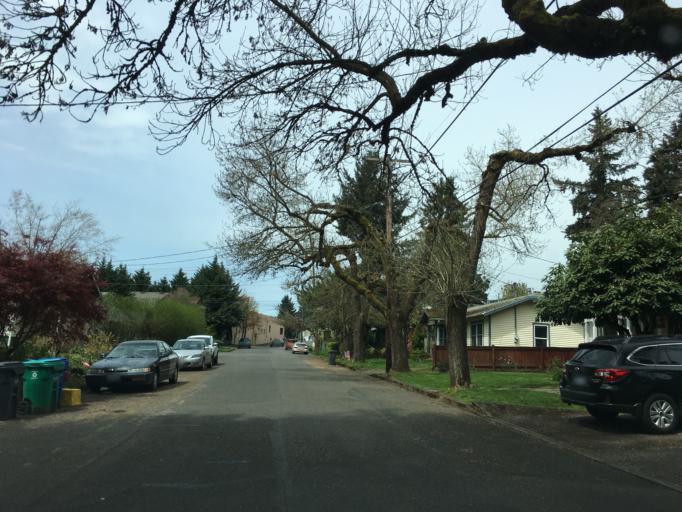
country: US
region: Oregon
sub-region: Multnomah County
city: Lents
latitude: 45.5541
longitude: -122.5707
